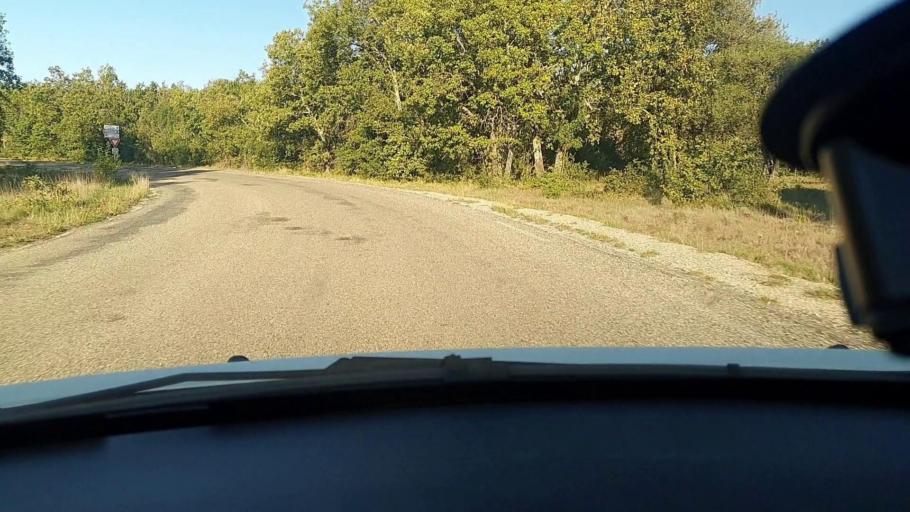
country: FR
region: Languedoc-Roussillon
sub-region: Departement du Gard
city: Barjac
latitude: 44.2225
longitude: 4.3235
